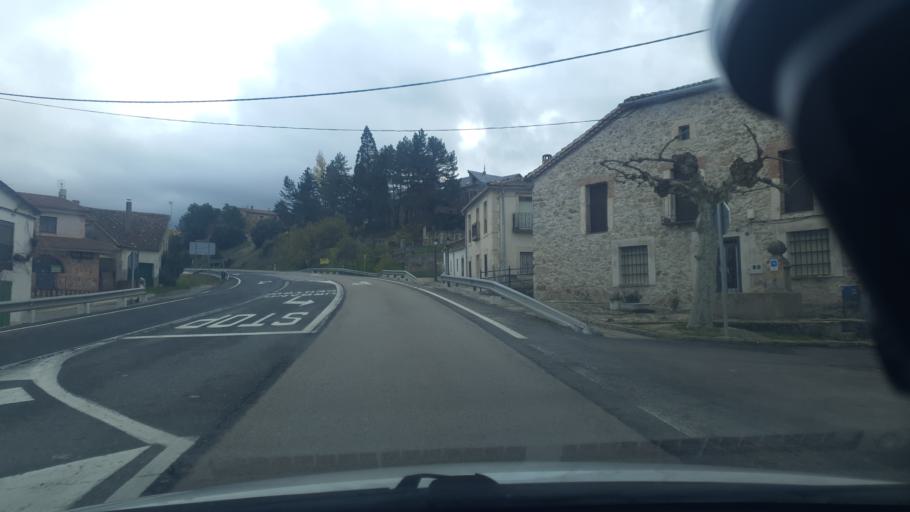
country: ES
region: Castille and Leon
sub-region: Provincia de Segovia
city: Cerezo de Abajo
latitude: 41.2178
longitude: -3.5906
